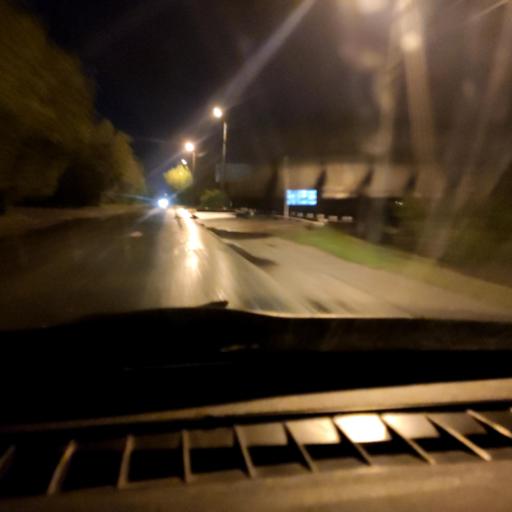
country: RU
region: Samara
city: Syzran'
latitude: 53.1703
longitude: 48.5084
